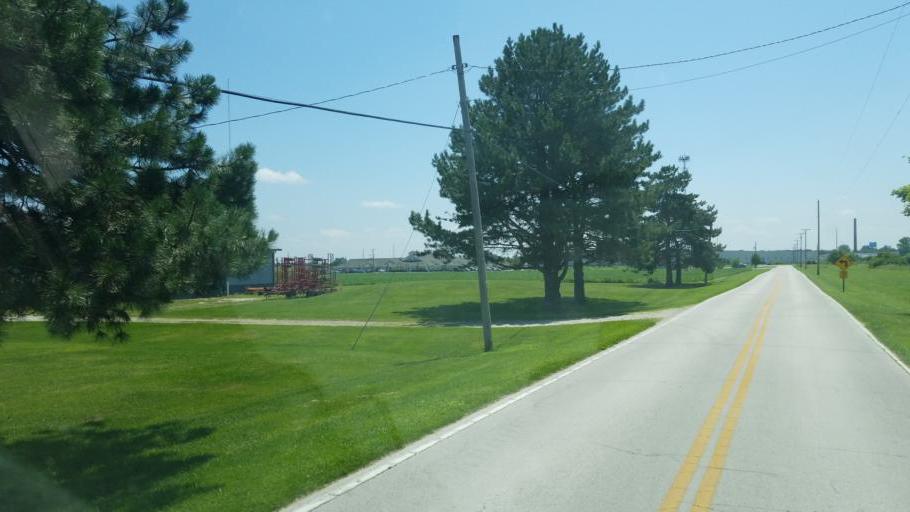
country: US
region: Ohio
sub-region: Sandusky County
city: Fremont
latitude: 41.3690
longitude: -83.0927
